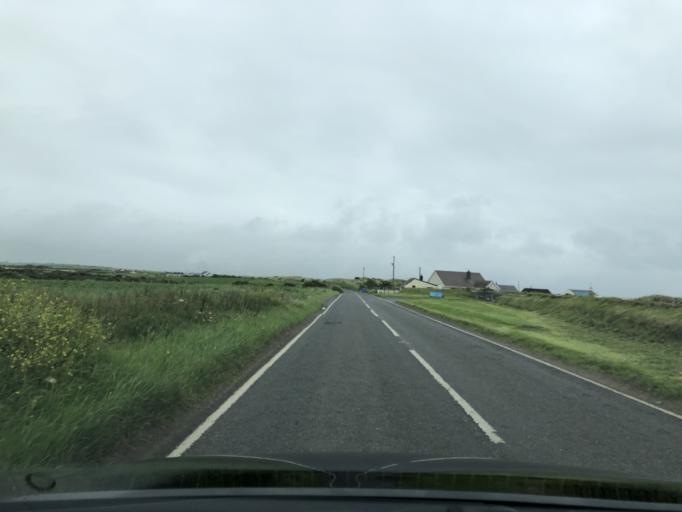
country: GB
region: Northern Ireland
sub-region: Down District
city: Downpatrick
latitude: 54.2544
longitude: -5.7490
